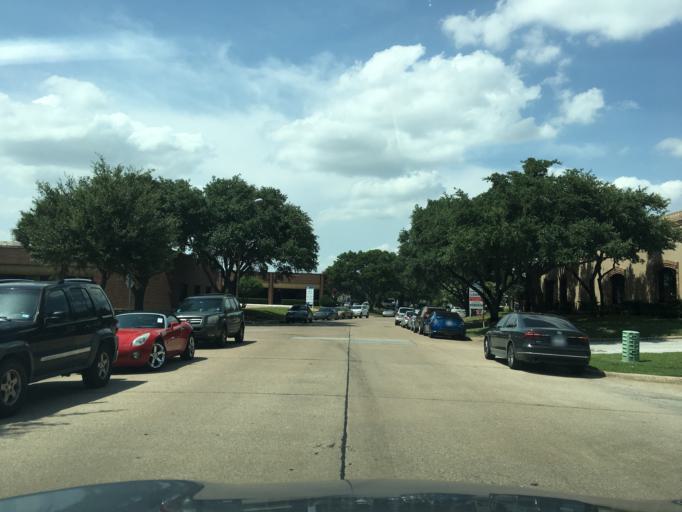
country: US
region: Texas
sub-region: Dallas County
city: Addison
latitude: 32.9499
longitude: -96.8325
